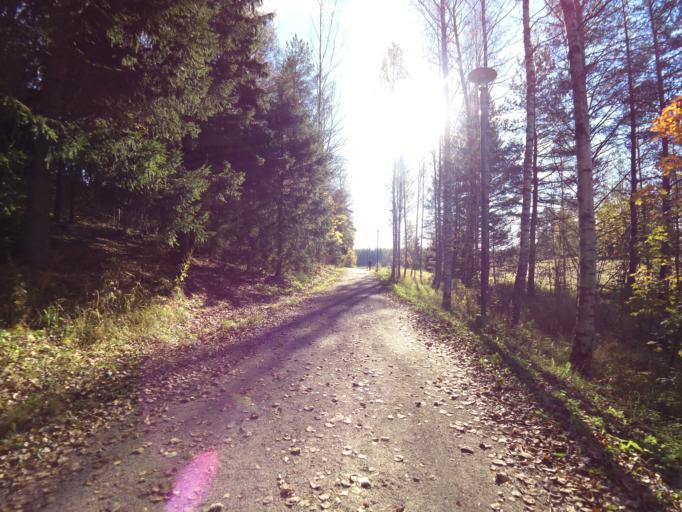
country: FI
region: Uusimaa
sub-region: Helsinki
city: Espoo
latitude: 60.1924
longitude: 24.6745
